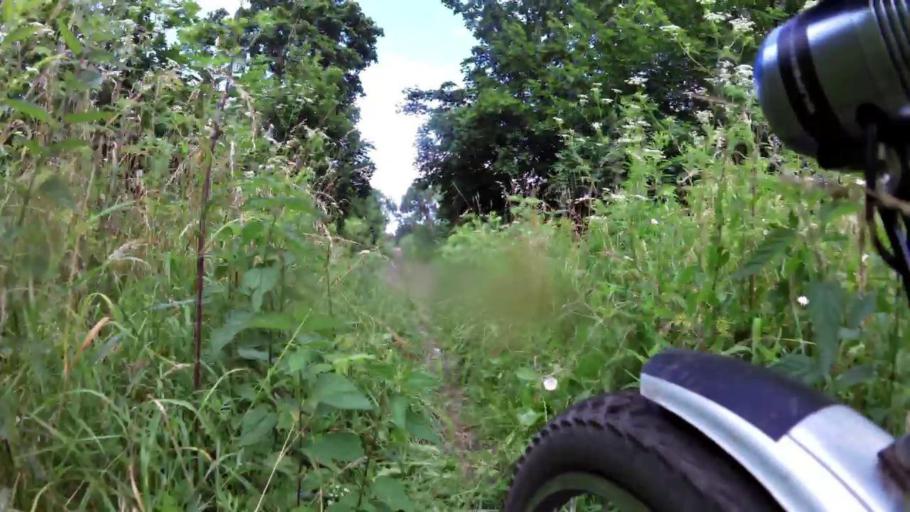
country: PL
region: West Pomeranian Voivodeship
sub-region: Powiat bialogardzki
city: Bialogard
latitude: 53.9997
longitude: 15.9853
